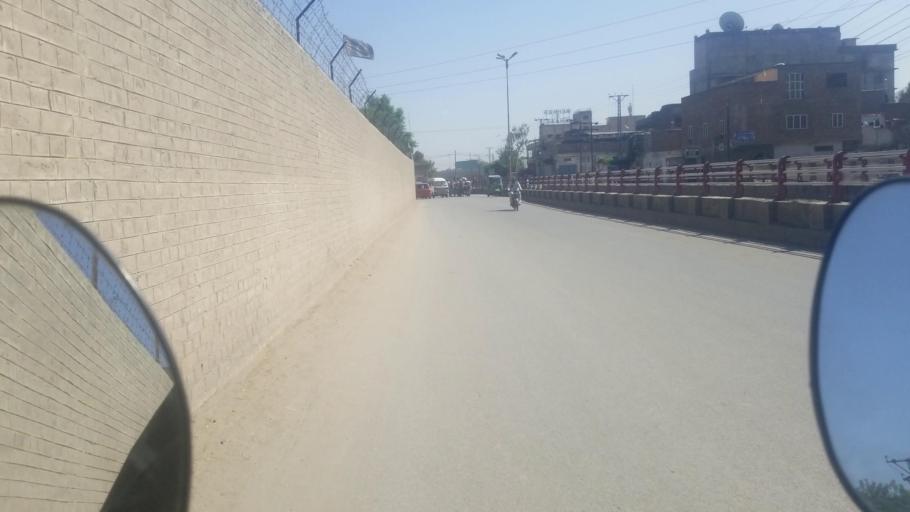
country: PK
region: Khyber Pakhtunkhwa
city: Peshawar
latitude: 34.0191
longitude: 71.5927
